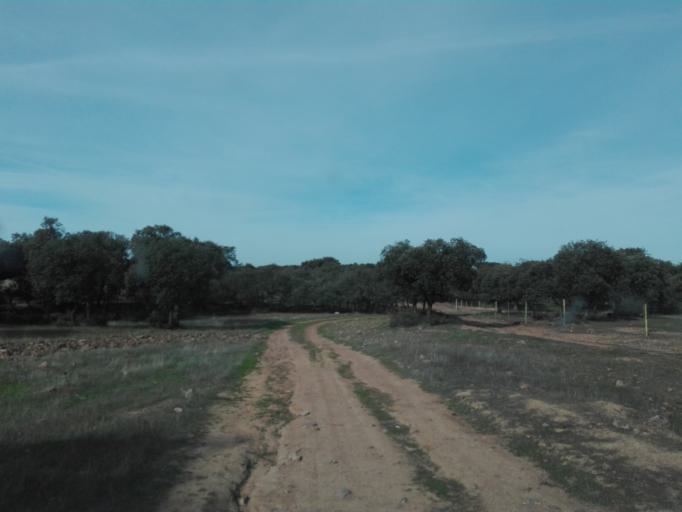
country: ES
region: Extremadura
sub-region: Provincia de Badajoz
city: Campillo de Llerena
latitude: 38.4692
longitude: -5.8890
